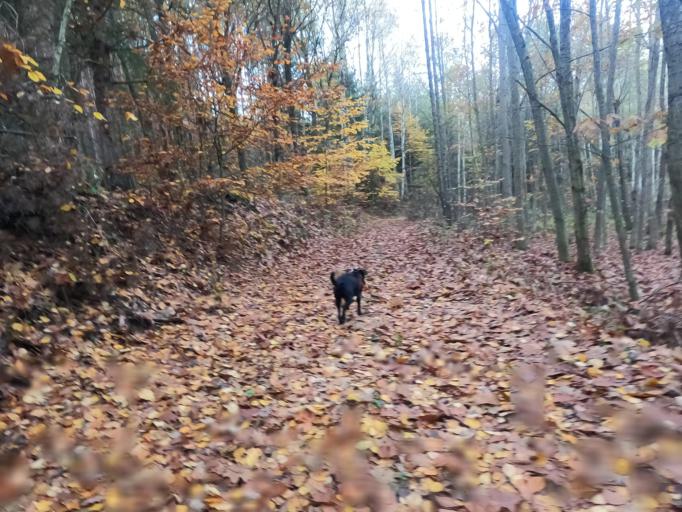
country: PL
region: Pomeranian Voivodeship
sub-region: Powiat starogardzki
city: Skarszewy
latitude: 54.0083
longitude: 18.4589
